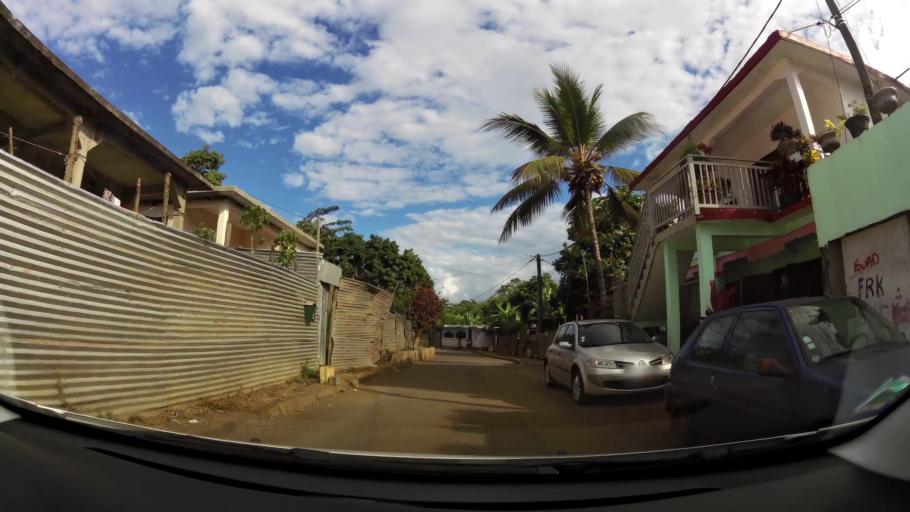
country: YT
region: Ouangani
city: Ouangani
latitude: -12.8395
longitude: 45.1304
